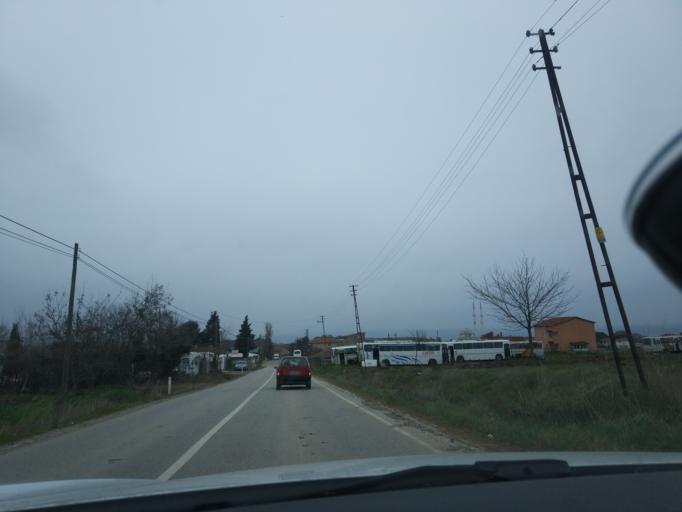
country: TR
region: Tekirdag
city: Marmara Ereglisi
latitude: 41.0172
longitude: 27.8524
